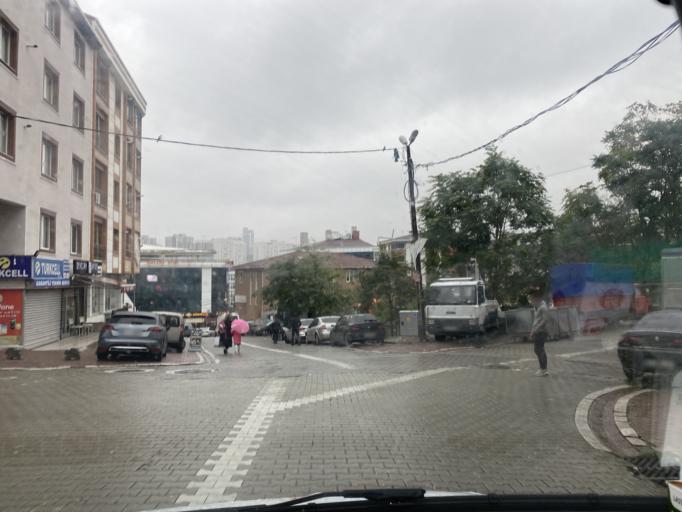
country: TR
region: Istanbul
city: Esenyurt
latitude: 41.0184
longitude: 28.6638
